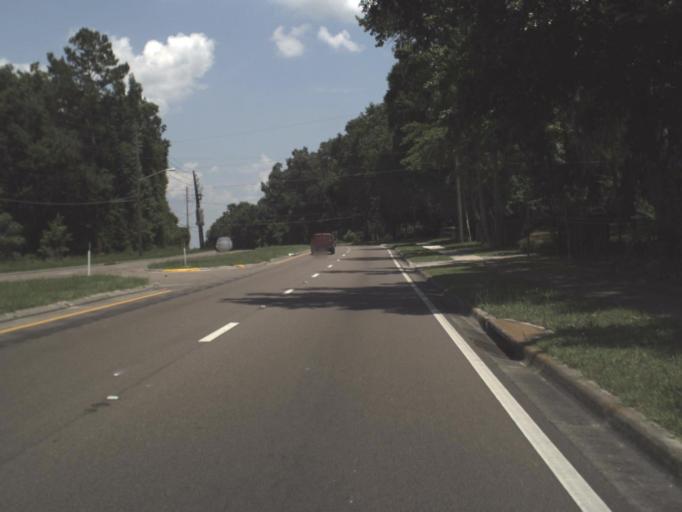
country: US
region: Florida
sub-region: Alachua County
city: Alachua
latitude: 29.6601
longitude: -82.4300
